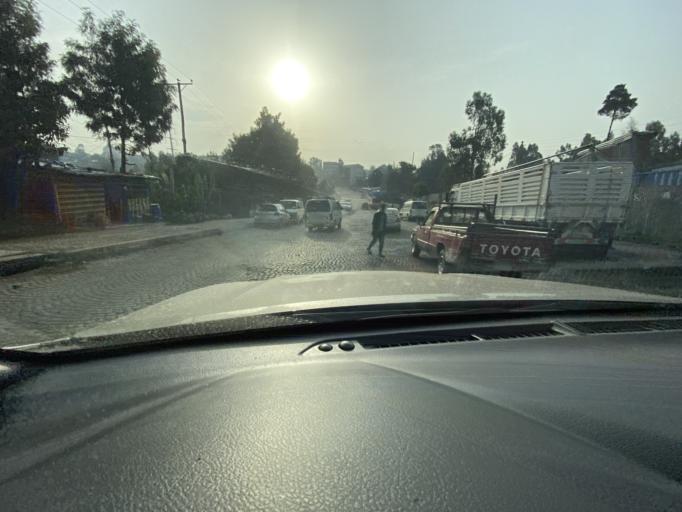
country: ET
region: Adis Abeba
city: Addis Ababa
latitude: 9.0215
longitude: 38.7177
